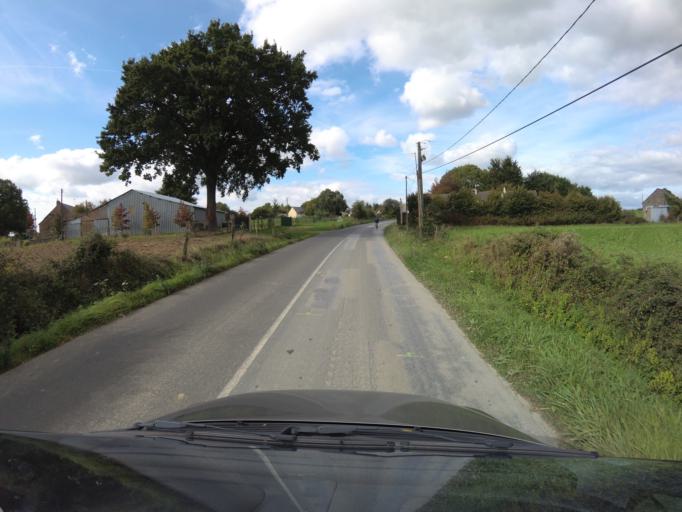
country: FR
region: Pays de la Loire
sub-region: Departement de la Loire-Atlantique
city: Casson
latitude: 47.3959
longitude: -1.5661
